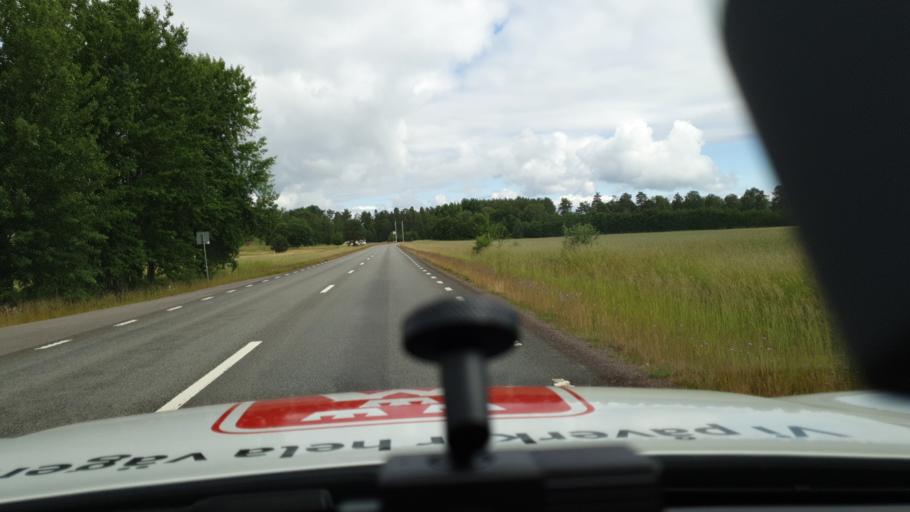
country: SE
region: Vaestra Goetaland
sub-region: Karlsborgs Kommun
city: Molltorp
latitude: 58.4409
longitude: 14.3993
